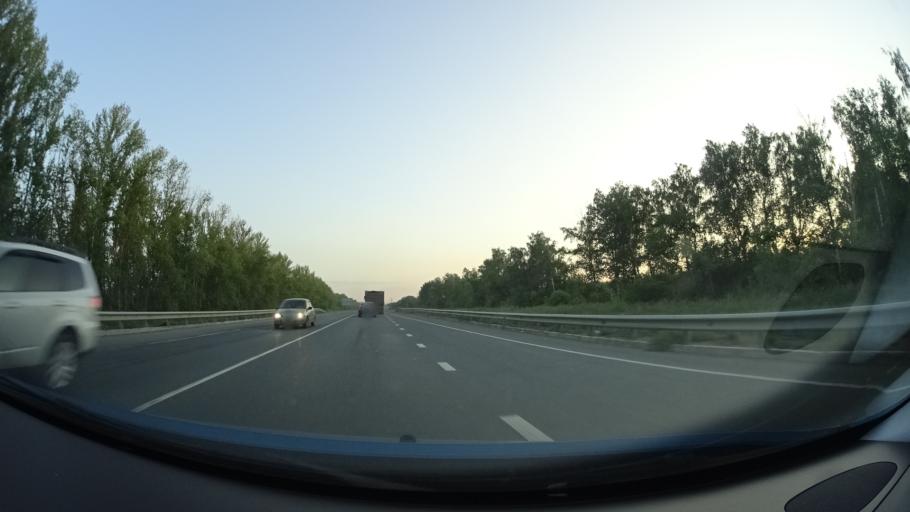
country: RU
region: Samara
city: Sukhodol
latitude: 53.8712
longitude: 51.2037
